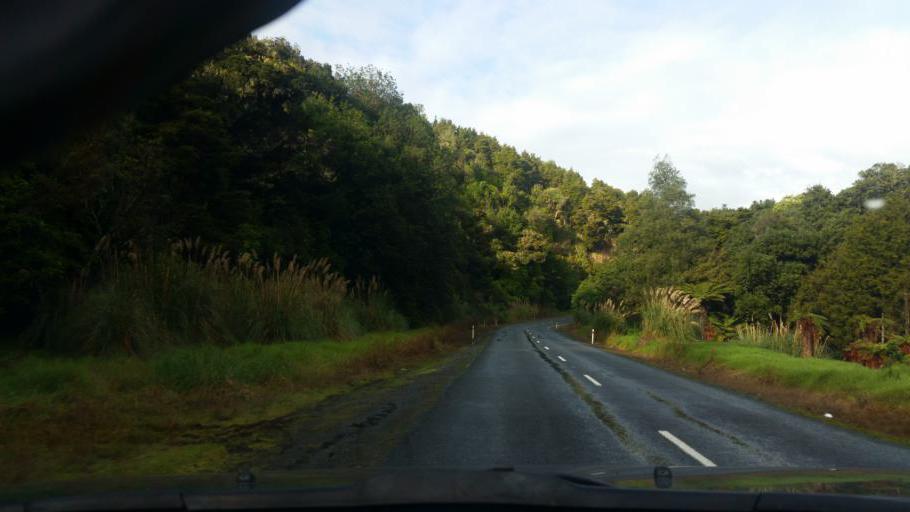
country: NZ
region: Northland
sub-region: Kaipara District
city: Dargaville
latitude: -35.7721
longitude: 173.9090
